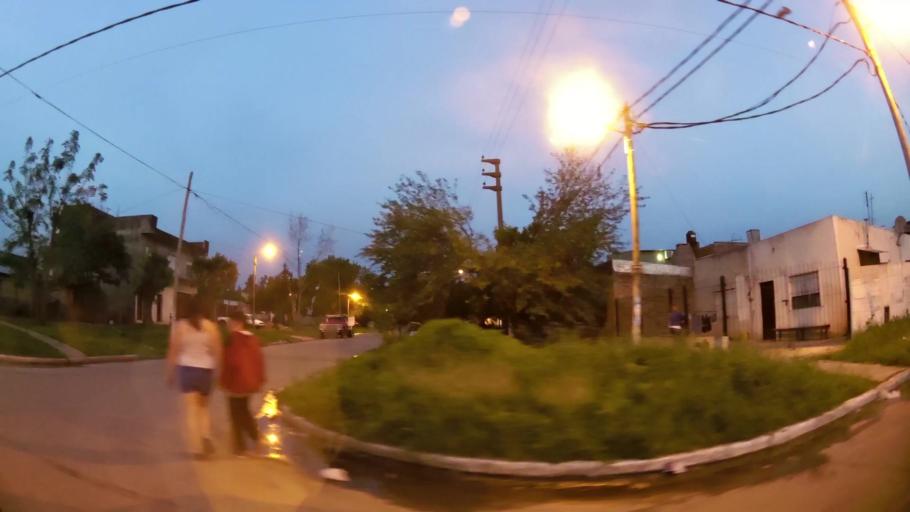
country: AR
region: Buenos Aires
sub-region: Partido de Quilmes
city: Quilmes
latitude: -34.8052
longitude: -58.2897
